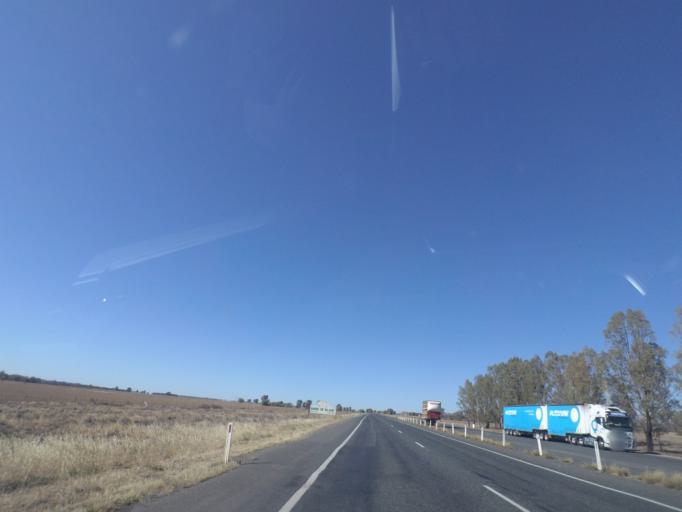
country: AU
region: New South Wales
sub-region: Bland
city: West Wyalong
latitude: -33.7667
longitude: 147.5171
